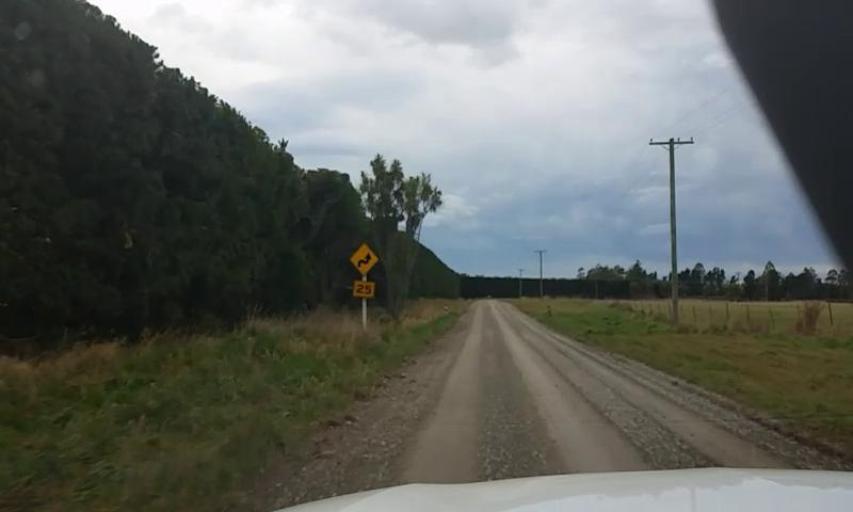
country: NZ
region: Canterbury
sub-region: Waimakariri District
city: Kaiapoi
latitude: -43.2908
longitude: 172.4437
